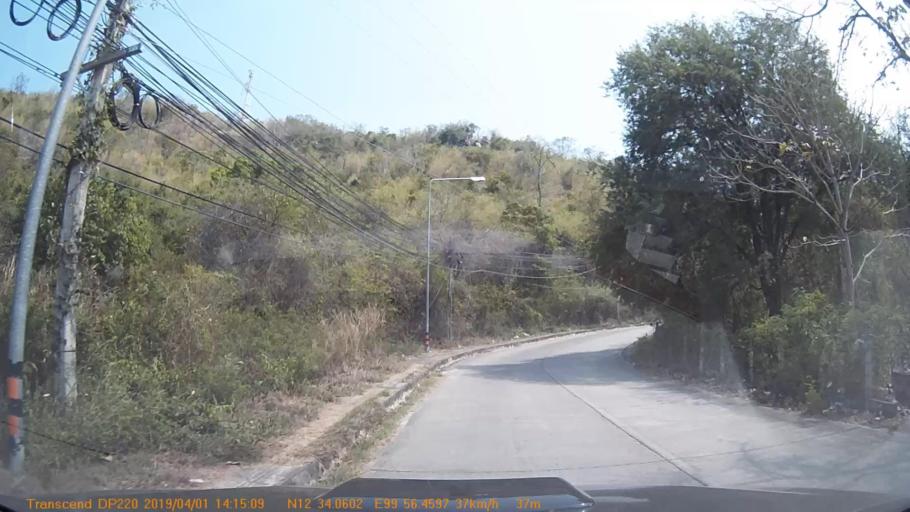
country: TH
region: Prachuap Khiri Khan
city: Hua Hin
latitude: 12.5676
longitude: 99.9410
